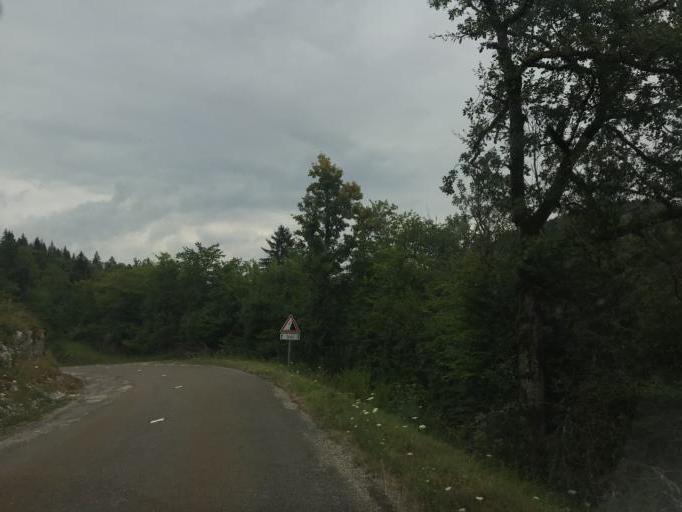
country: FR
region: Franche-Comte
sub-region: Departement du Jura
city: Lavans-les-Saint-Claude
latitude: 46.3249
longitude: 5.7593
